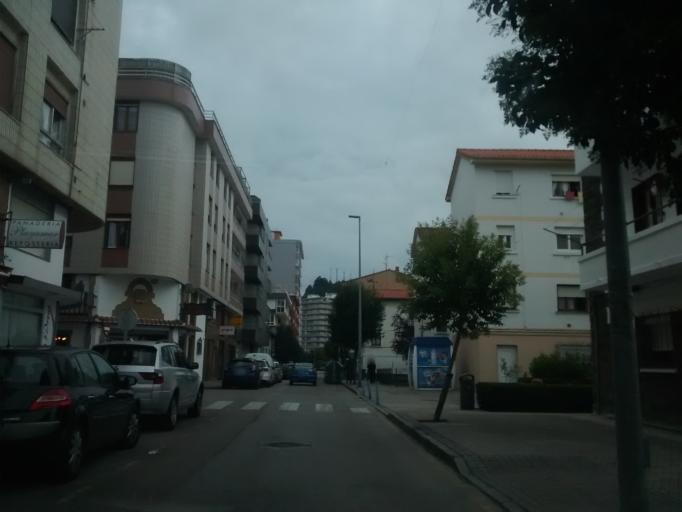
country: ES
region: Cantabria
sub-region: Provincia de Cantabria
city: Laredo
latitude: 43.4128
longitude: -3.4156
